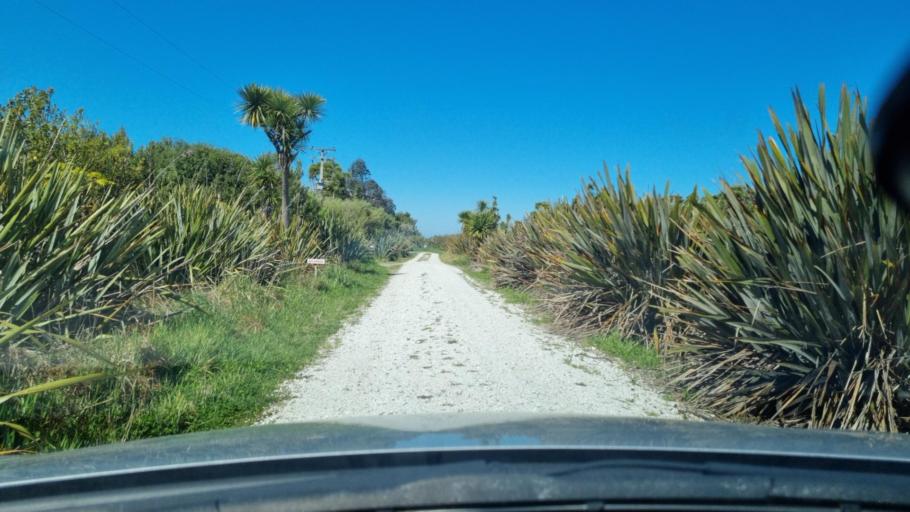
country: NZ
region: Southland
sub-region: Invercargill City
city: Invercargill
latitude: -46.4524
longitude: 168.3166
